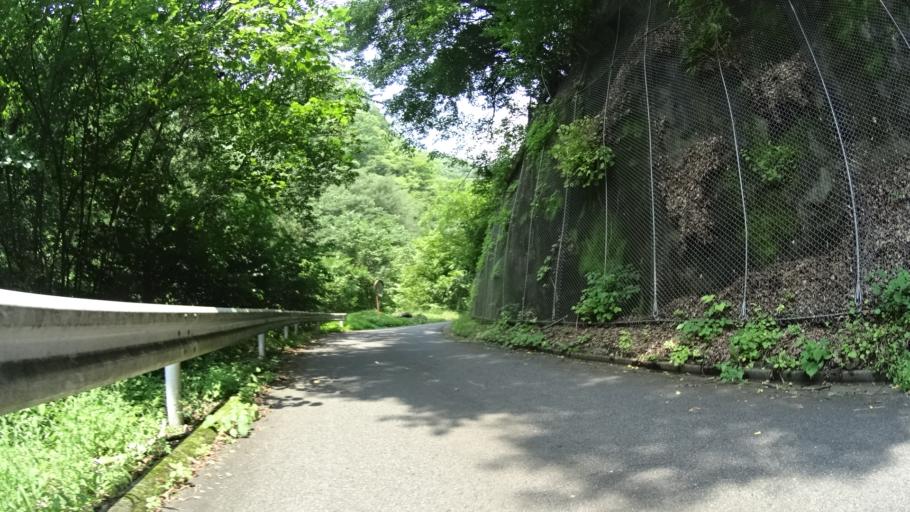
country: JP
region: Gunma
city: Tomioka
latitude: 36.0822
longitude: 138.7080
